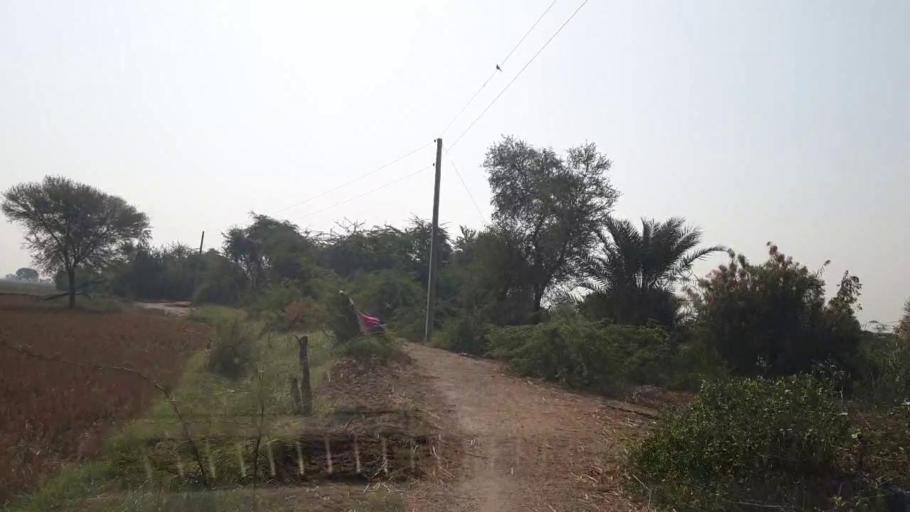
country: PK
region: Sindh
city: Matli
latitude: 24.9744
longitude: 68.6152
